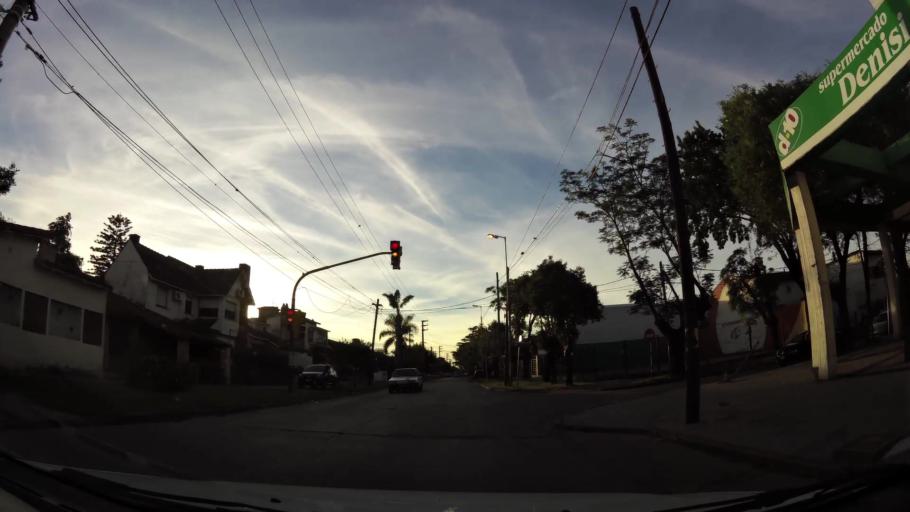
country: AR
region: Buenos Aires
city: Ituzaingo
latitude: -34.6428
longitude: -58.6409
